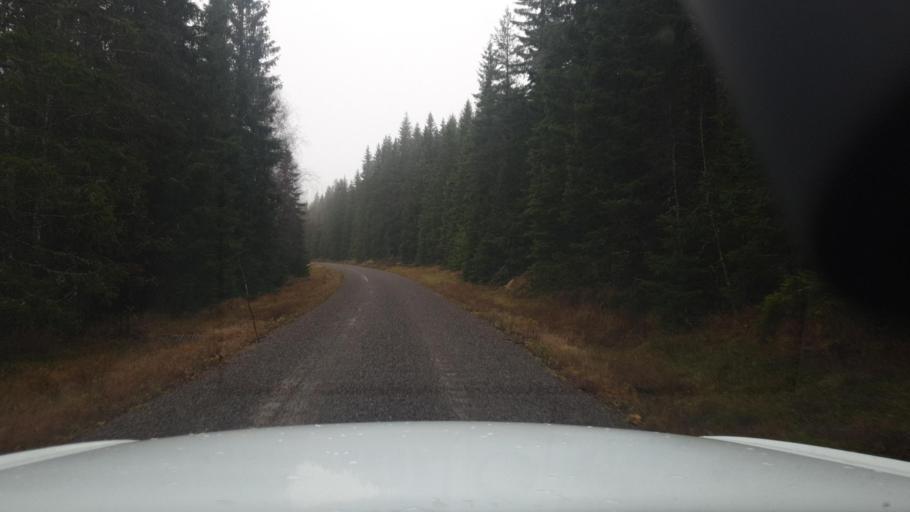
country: SE
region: Vaermland
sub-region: Eda Kommun
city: Charlottenberg
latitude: 60.0806
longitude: 12.6196
